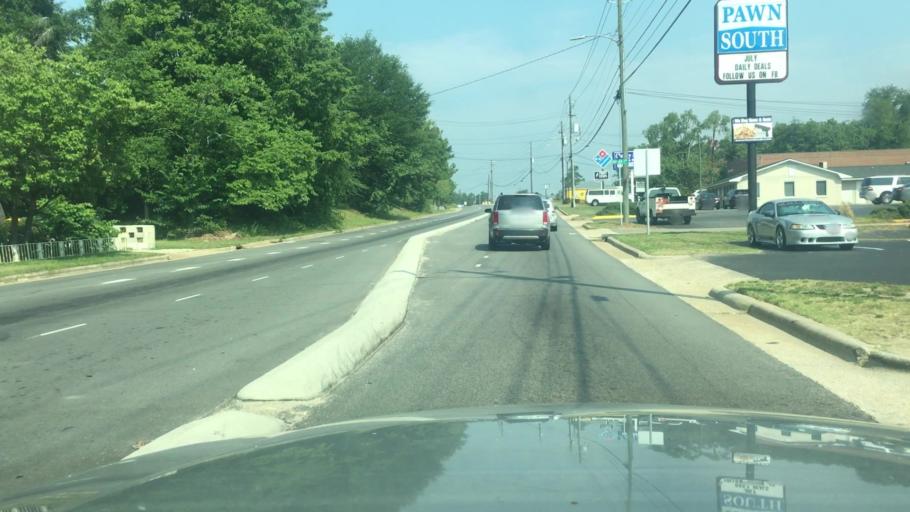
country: US
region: North Carolina
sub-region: Cumberland County
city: Hope Mills
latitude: 34.9761
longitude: -78.9513
